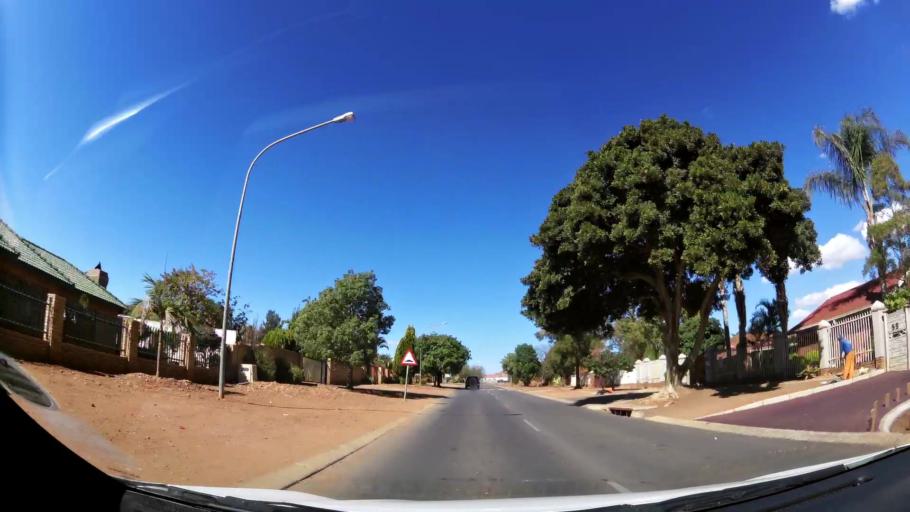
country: ZA
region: Limpopo
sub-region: Capricorn District Municipality
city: Polokwane
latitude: -23.9111
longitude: 29.4924
